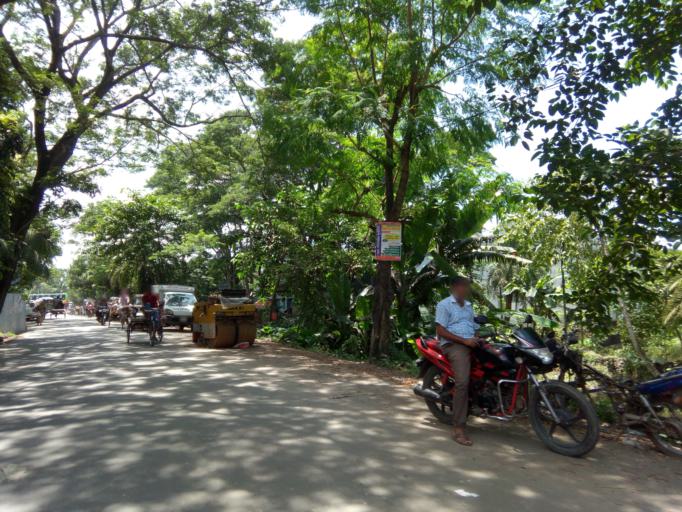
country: BD
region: Dhaka
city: Tungipara
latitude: 22.8958
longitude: 89.8908
